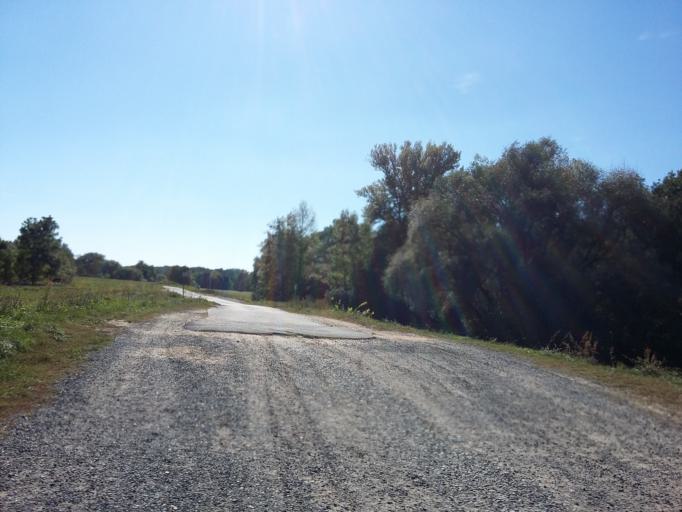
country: AT
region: Lower Austria
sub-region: Politischer Bezirk Ganserndorf
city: Marchegg
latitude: 48.3223
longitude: 16.9097
